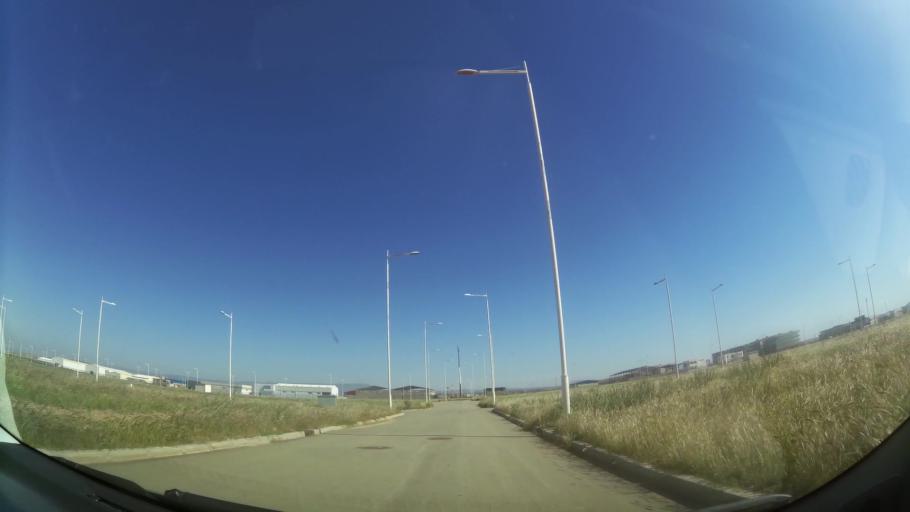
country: MA
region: Oriental
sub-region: Oujda-Angad
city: Oujda
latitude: 34.7734
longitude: -1.9355
